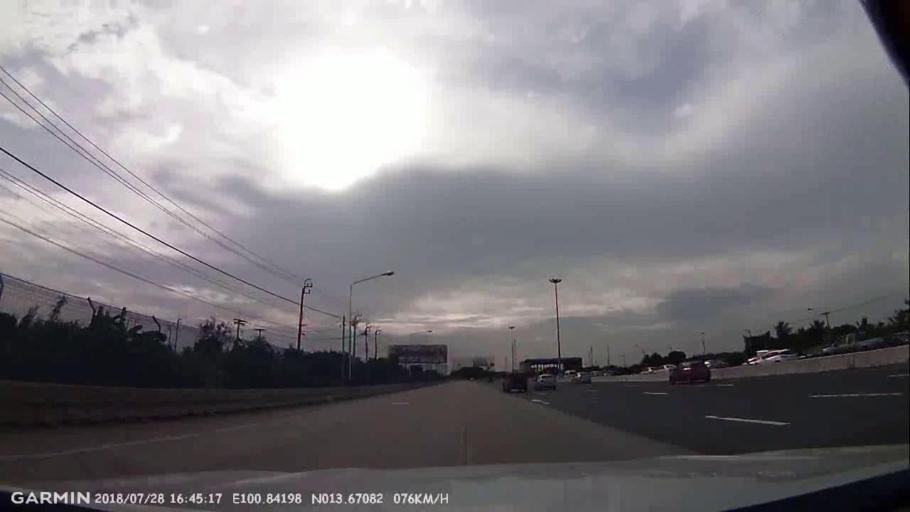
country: TH
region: Samut Prakan
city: Ban Khlong Bang Sao Thong
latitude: 13.6709
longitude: 100.8416
